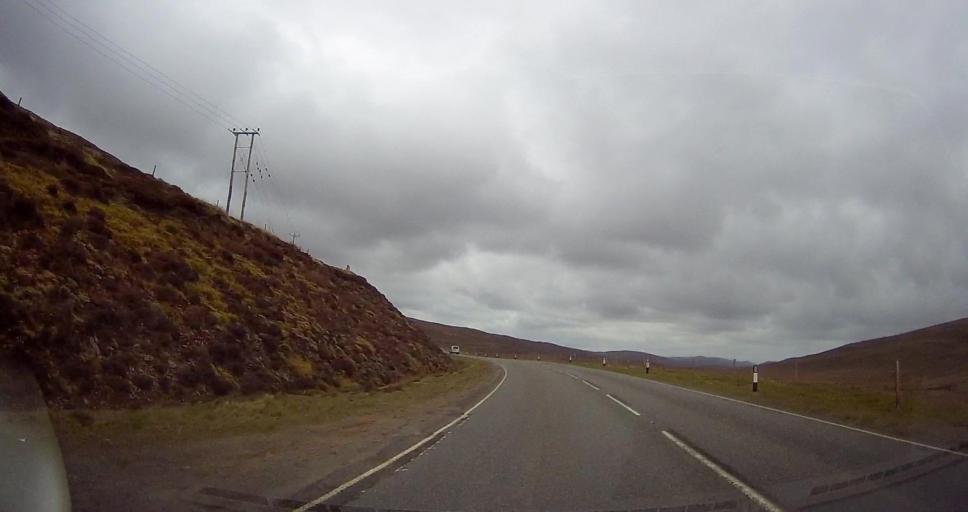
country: GB
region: Scotland
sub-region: Shetland Islands
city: Lerwick
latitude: 60.3124
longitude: -1.2467
